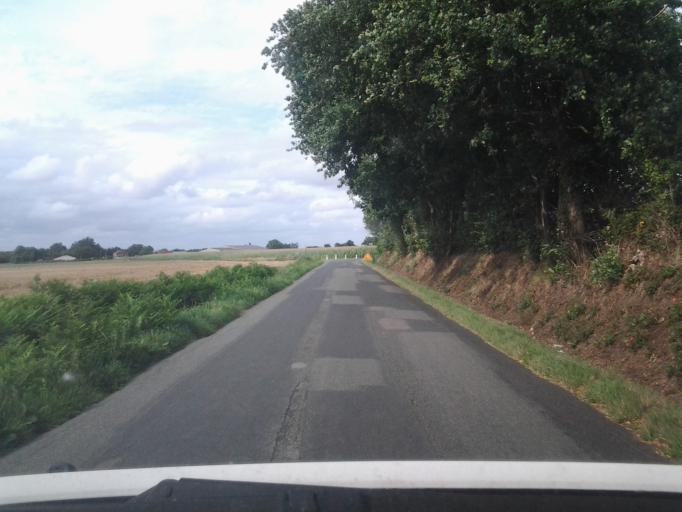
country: FR
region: Pays de la Loire
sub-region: Departement de la Vendee
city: Dompierre-sur-Yon
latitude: 46.6978
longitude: -1.3687
